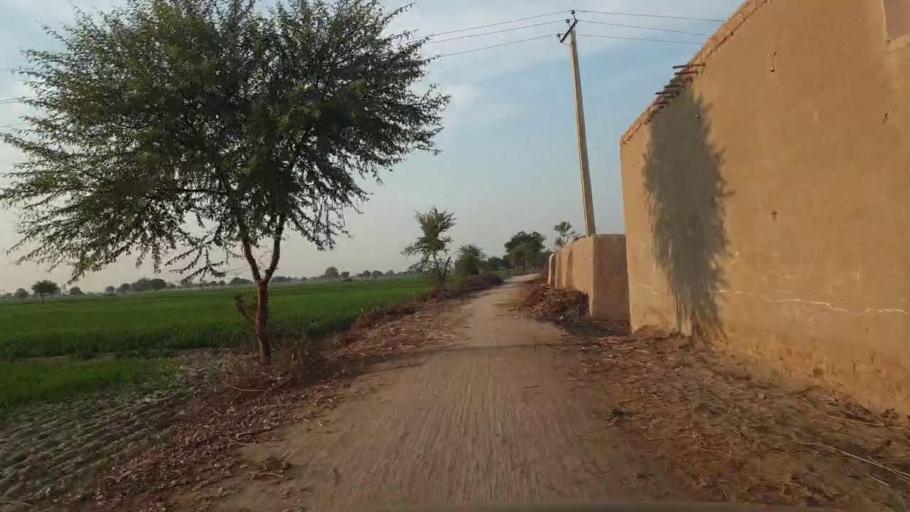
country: PK
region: Sindh
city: Shahpur Chakar
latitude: 26.1726
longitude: 68.6227
